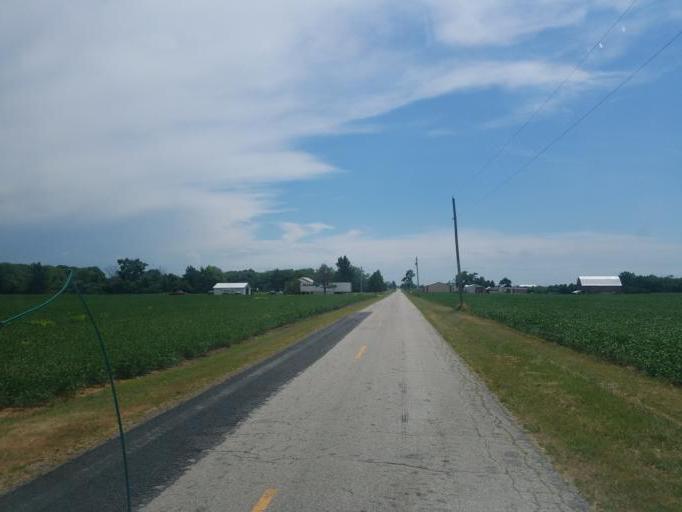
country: US
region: Ohio
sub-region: Paulding County
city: Antwerp
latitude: 41.2320
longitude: -84.7277
